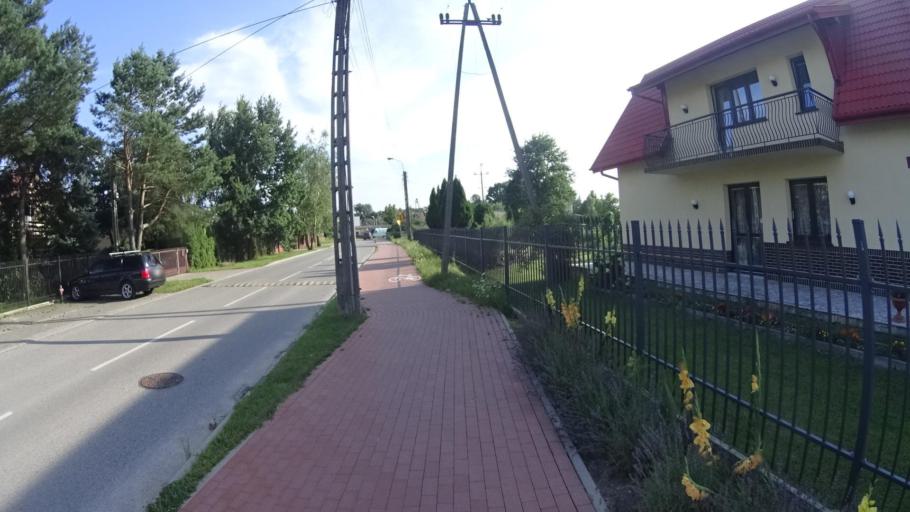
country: PL
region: Masovian Voivodeship
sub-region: Powiat pruszkowski
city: Nadarzyn
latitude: 52.0934
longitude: 20.7999
